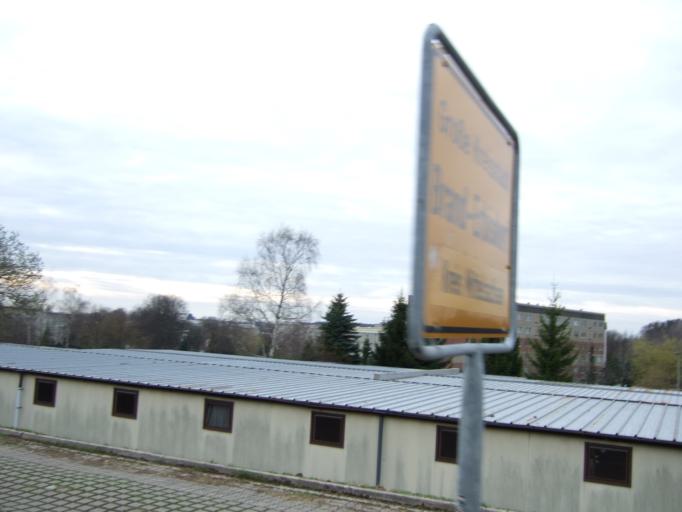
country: DE
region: Saxony
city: Brand-Erbisdorf
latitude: 50.8733
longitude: 13.3329
